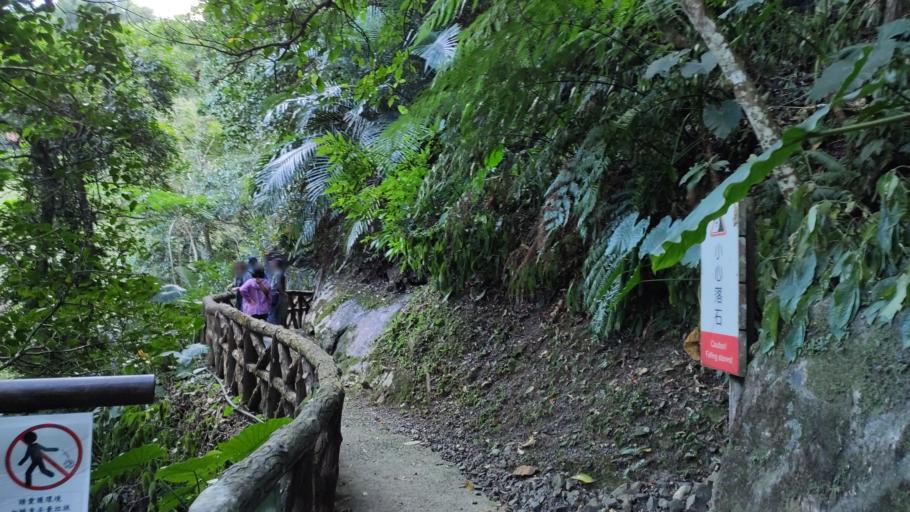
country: TW
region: Taiwan
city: Daxi
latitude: 24.7893
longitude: 121.3747
